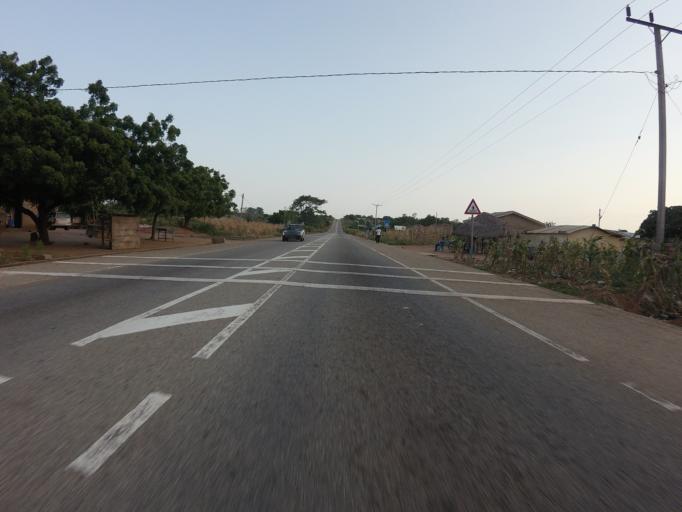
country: GH
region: Volta
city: Anloga
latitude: 6.0469
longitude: 0.6046
